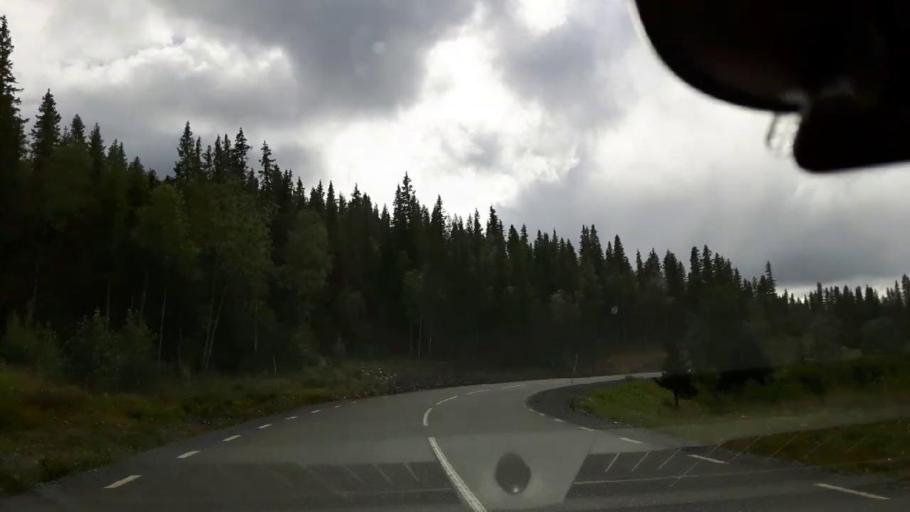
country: SE
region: Jaemtland
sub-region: Krokoms Kommun
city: Valla
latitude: 63.4864
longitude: 13.8609
